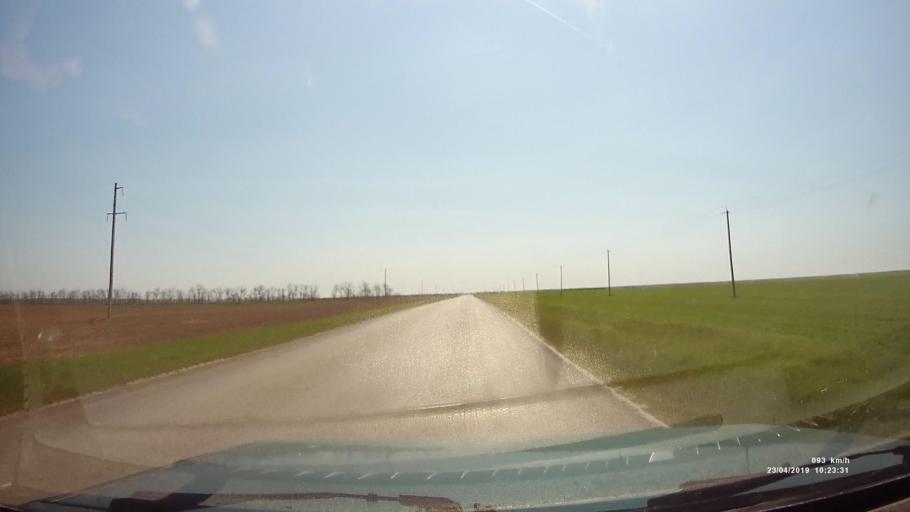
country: RU
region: Rostov
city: Sovetskoye
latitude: 46.6470
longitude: 42.4256
